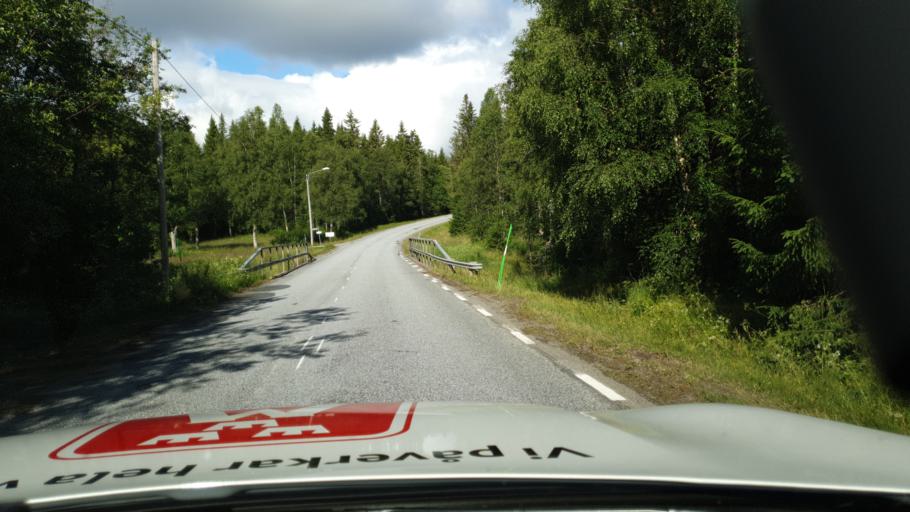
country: SE
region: Vaesterbotten
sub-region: Umea Kommun
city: Roback
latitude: 63.6738
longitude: 20.1147
